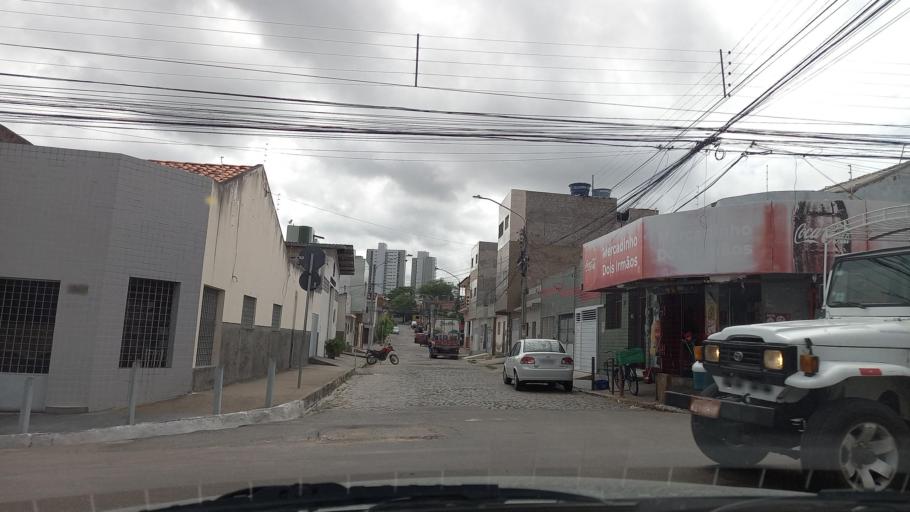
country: BR
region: Pernambuco
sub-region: Caruaru
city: Caruaru
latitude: -8.2781
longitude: -35.9791
